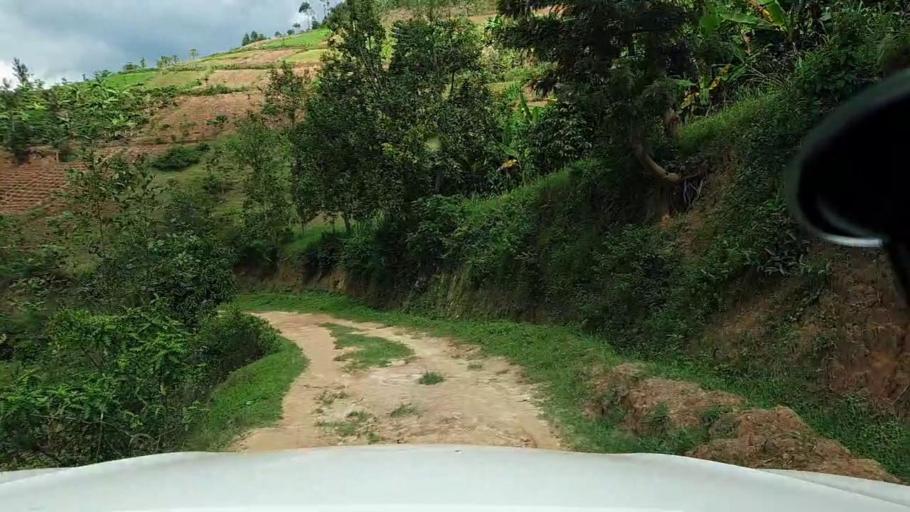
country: RW
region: Southern Province
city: Gitarama
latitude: -1.8175
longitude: 29.8010
